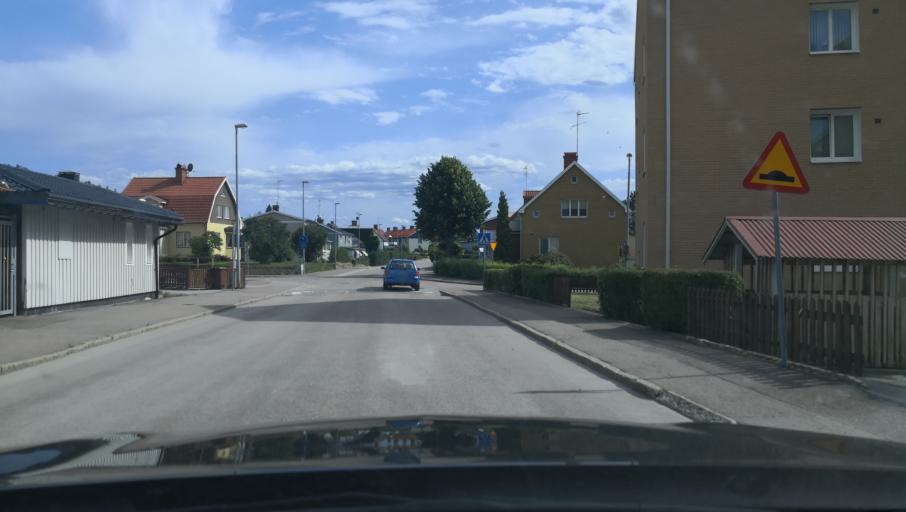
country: SE
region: Vaestmanland
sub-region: Fagersta Kommun
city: Fagersta
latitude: 59.9899
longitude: 15.8244
